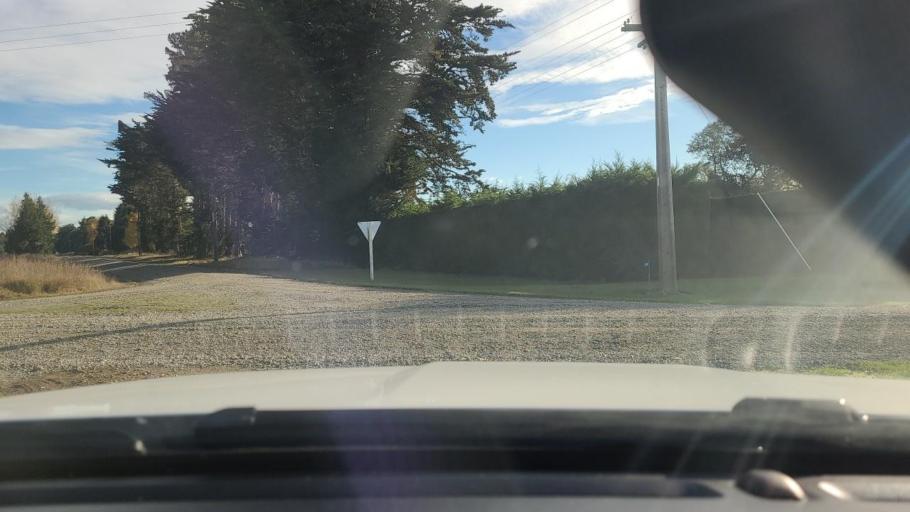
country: NZ
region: Southland
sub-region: Gore District
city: Gore
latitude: -45.9784
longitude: 168.8069
